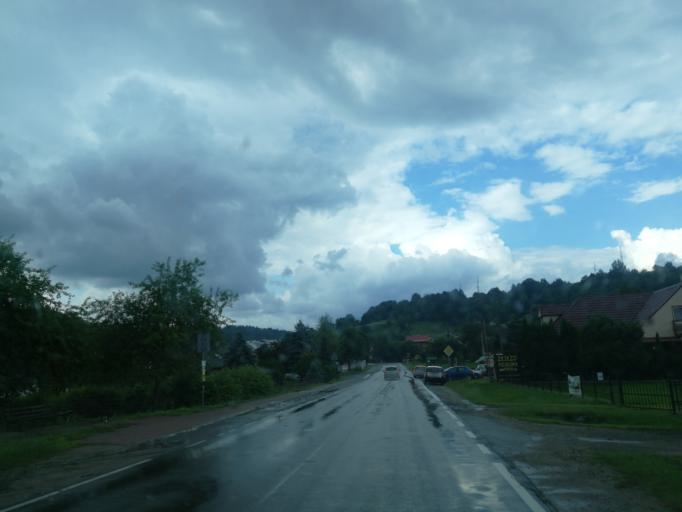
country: PL
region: Subcarpathian Voivodeship
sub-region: Powiat leski
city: Polanczyk
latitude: 49.4130
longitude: 22.4488
